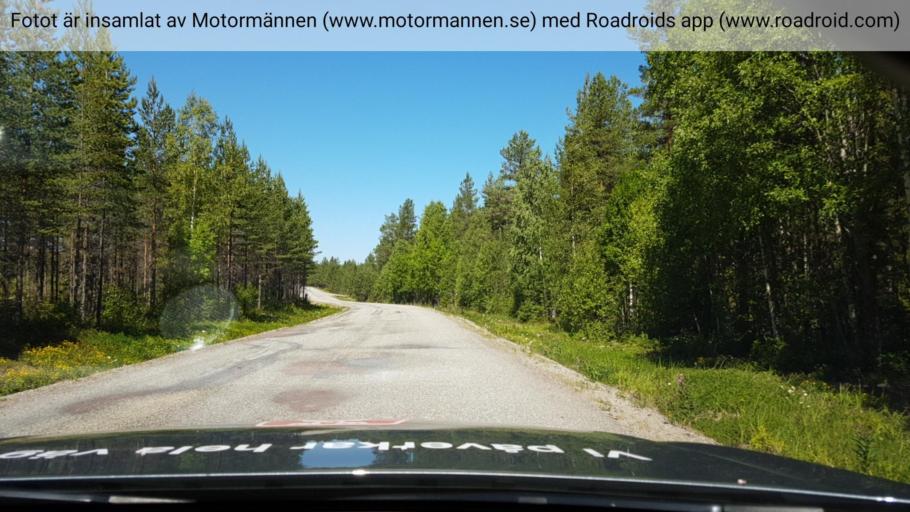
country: SE
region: Jaemtland
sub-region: Braecke Kommun
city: Braecke
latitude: 62.8956
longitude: 15.1615
